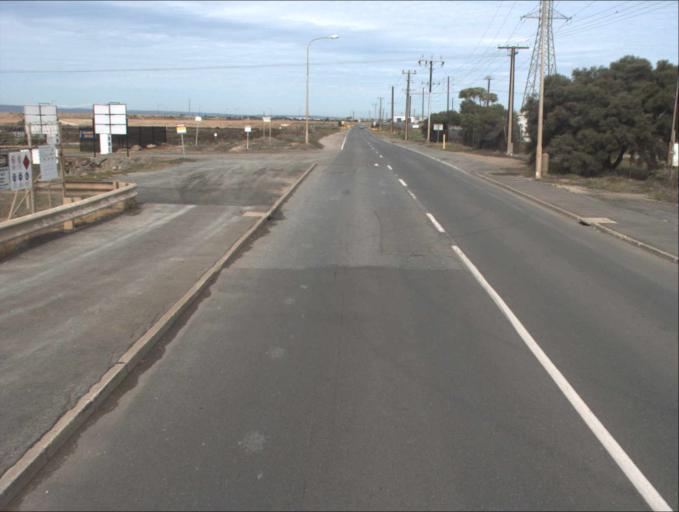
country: AU
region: South Australia
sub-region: Port Adelaide Enfield
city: Birkenhead
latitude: -34.8129
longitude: 138.5253
